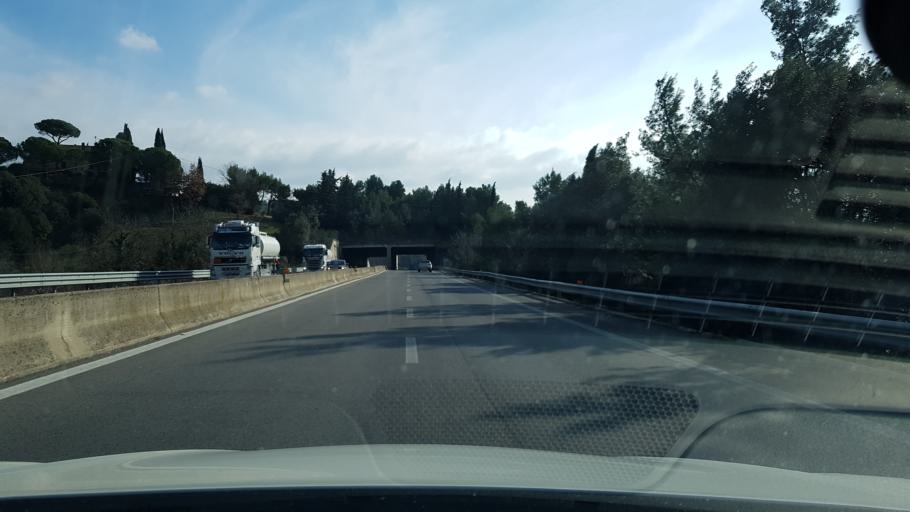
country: IT
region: Umbria
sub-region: Provincia di Perugia
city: Passignano sul Trasimeno
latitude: 43.1950
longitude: 12.1346
